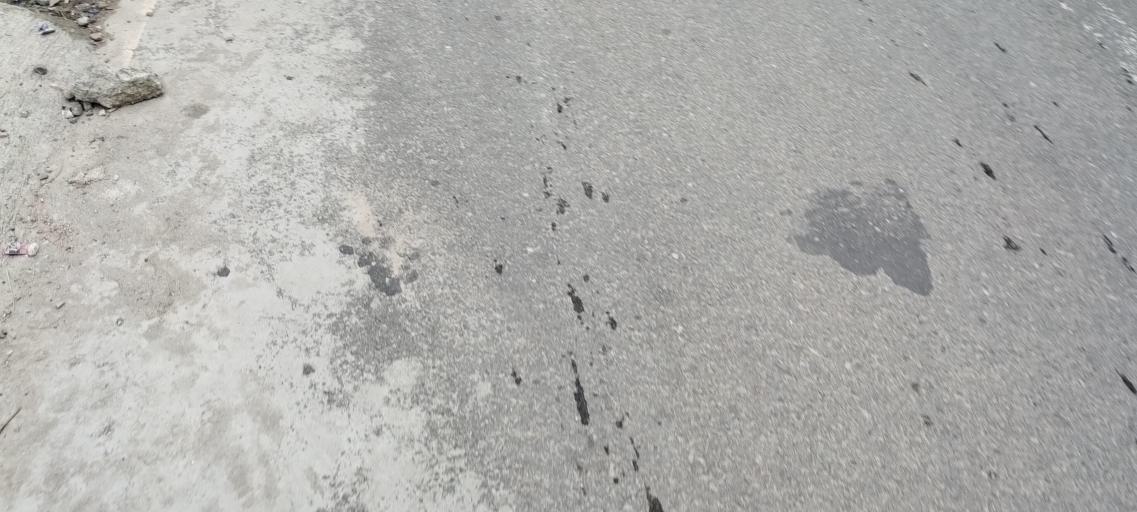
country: NP
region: Central Region
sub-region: Bagmati Zone
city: Kathmandu
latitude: 27.7811
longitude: 85.3638
